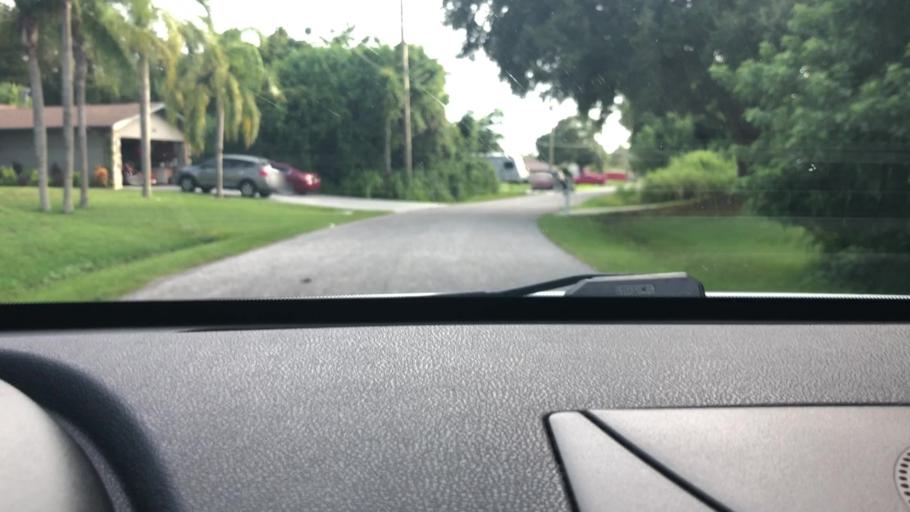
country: US
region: Florida
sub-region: Sarasota County
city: South Venice
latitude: 27.0437
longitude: -82.4111
